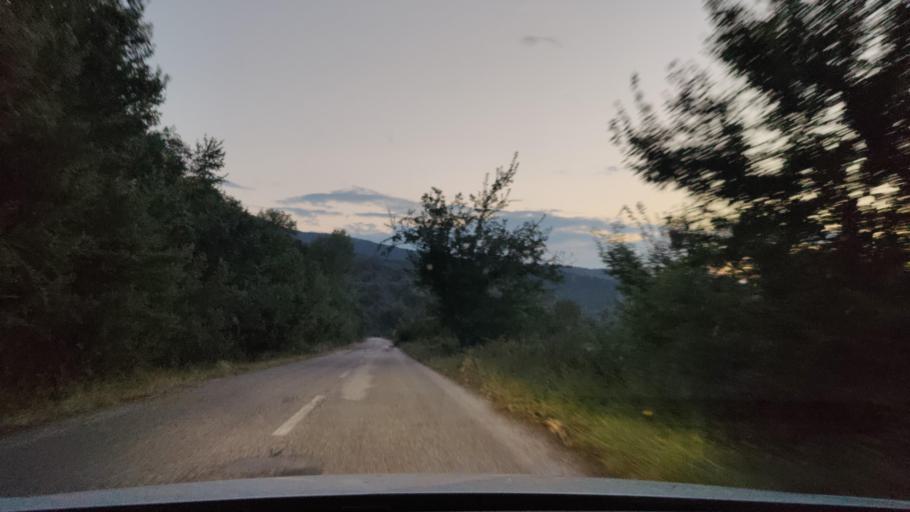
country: GR
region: Central Macedonia
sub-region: Nomos Serron
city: Chrysochorafa
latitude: 41.1975
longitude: 23.0878
